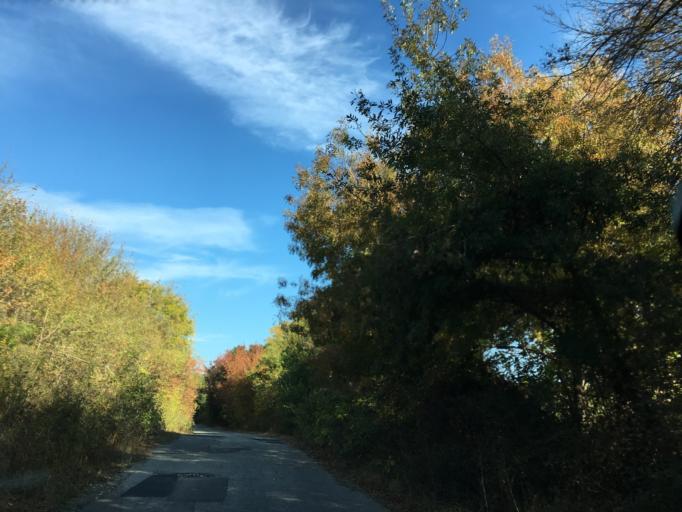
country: BG
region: Khaskovo
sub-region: Obshtina Ivaylovgrad
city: Ivaylovgrad
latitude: 41.3986
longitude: 26.1264
